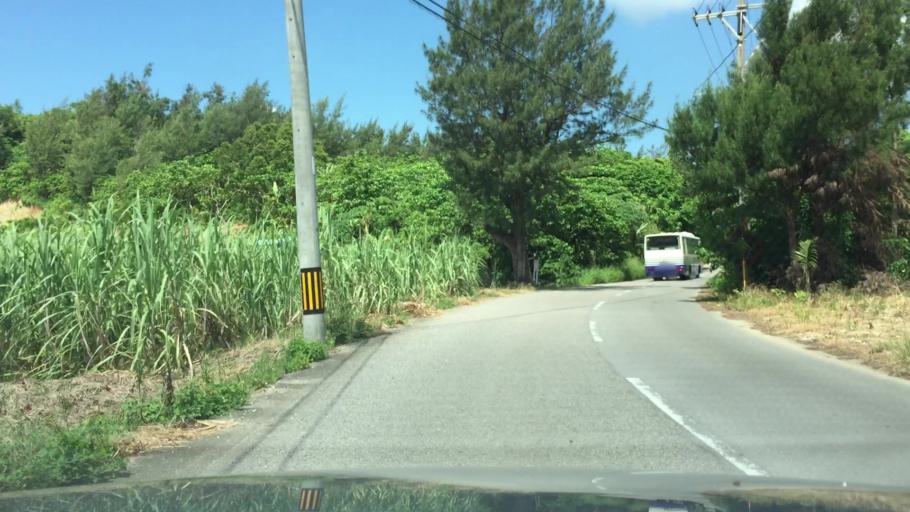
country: JP
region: Okinawa
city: Ishigaki
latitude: 24.3771
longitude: 124.1258
